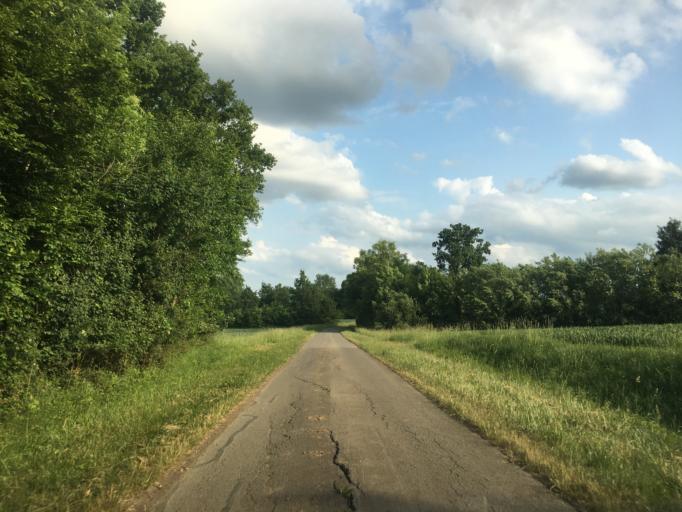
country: DE
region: North Rhine-Westphalia
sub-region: Regierungsbezirk Munster
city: Altenberge
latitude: 52.0247
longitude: 7.5407
